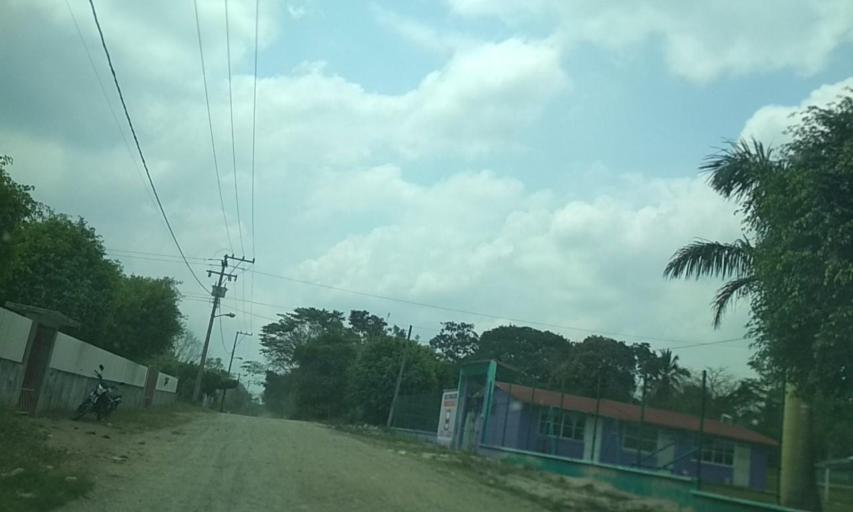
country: MX
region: Tabasco
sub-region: Huimanguillo
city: Francisco Rueda
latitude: 17.6010
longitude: -93.7969
